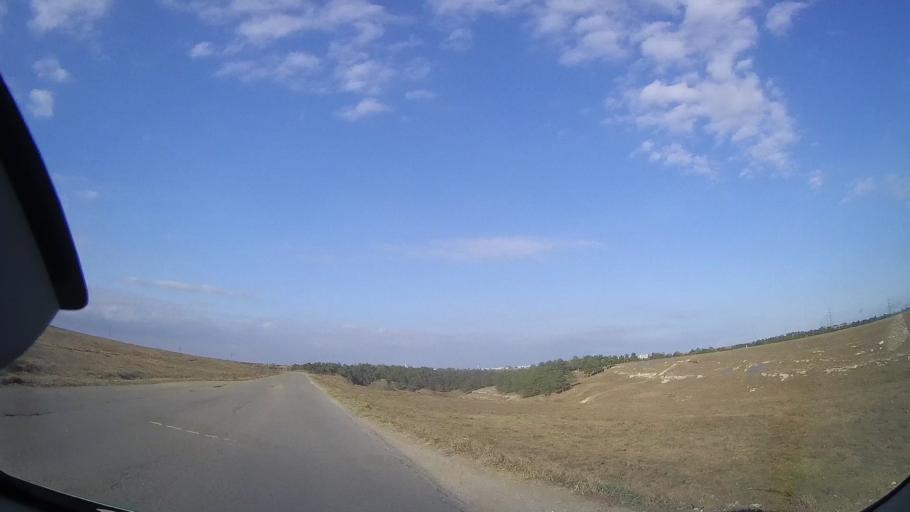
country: RO
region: Constanta
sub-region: Comuna Limanu
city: Limanu
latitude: 43.8067
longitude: 28.5202
